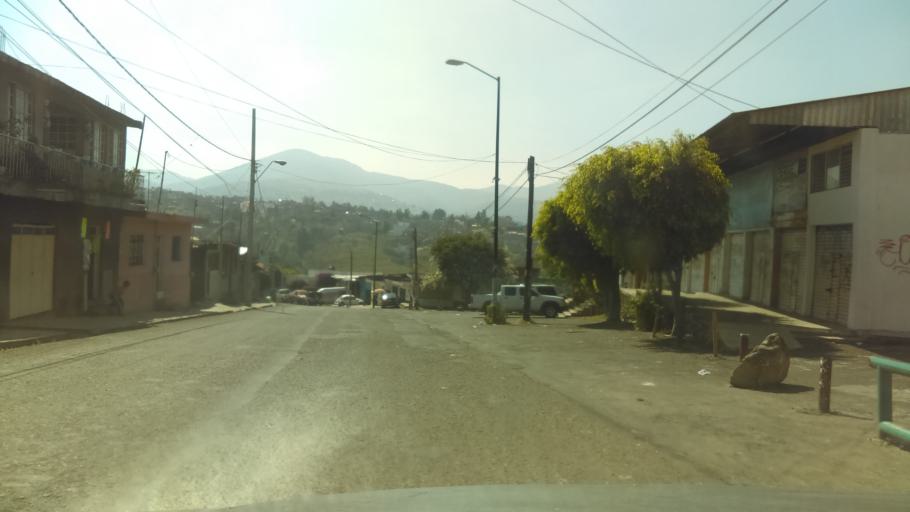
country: MX
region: Michoacan
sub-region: Morelia
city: Montana Monarca (Punta Altozano)
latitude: 19.6711
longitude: -101.1905
